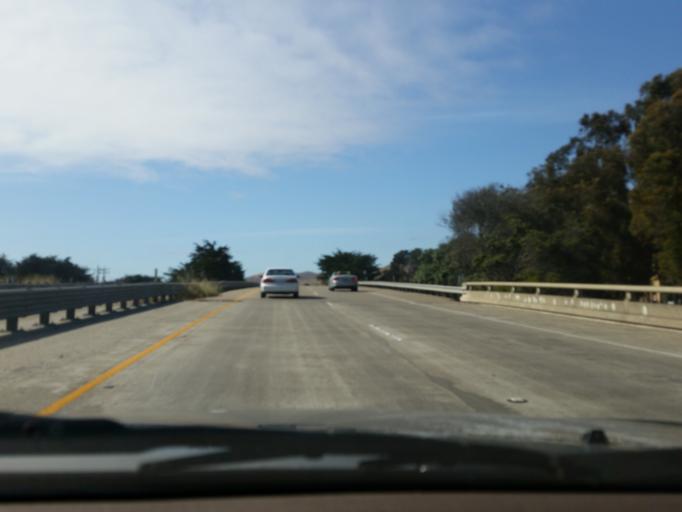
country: US
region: California
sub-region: San Luis Obispo County
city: Morro Bay
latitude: 35.3781
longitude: -120.8549
